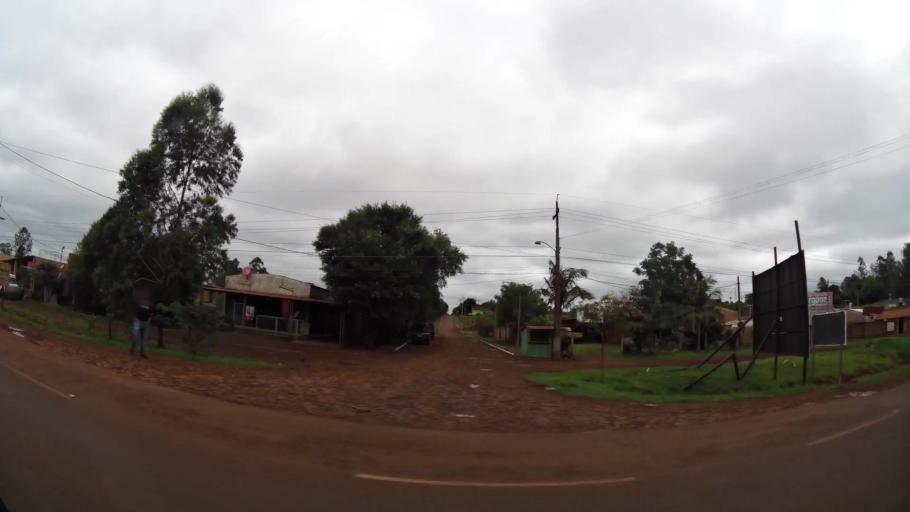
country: PY
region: Alto Parana
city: Presidente Franco
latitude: -25.4894
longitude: -54.8001
